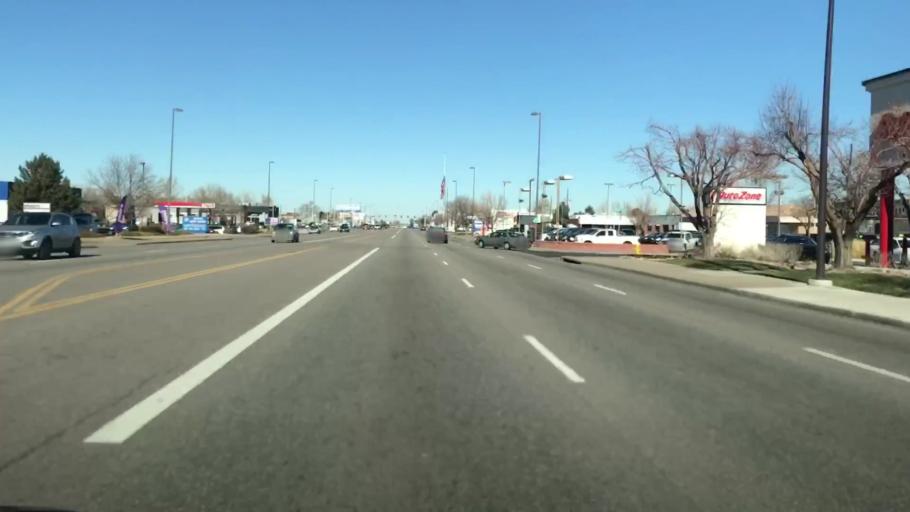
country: US
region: Colorado
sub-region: Adams County
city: Aurora
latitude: 39.6997
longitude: -104.8659
